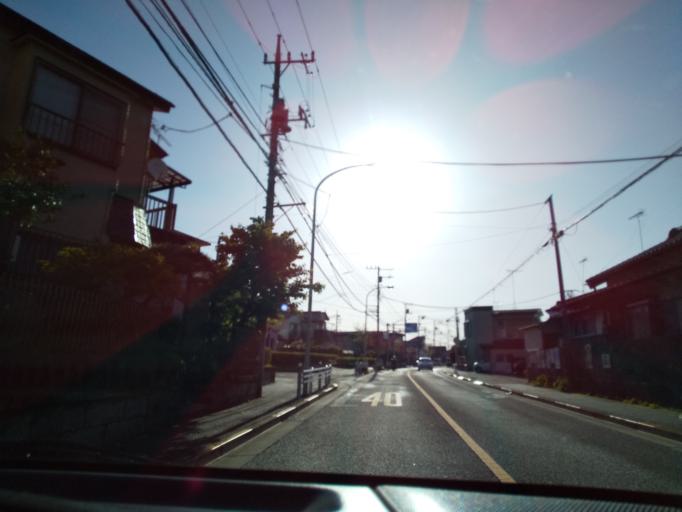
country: JP
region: Tokyo
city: Hino
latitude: 35.7013
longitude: 139.3812
